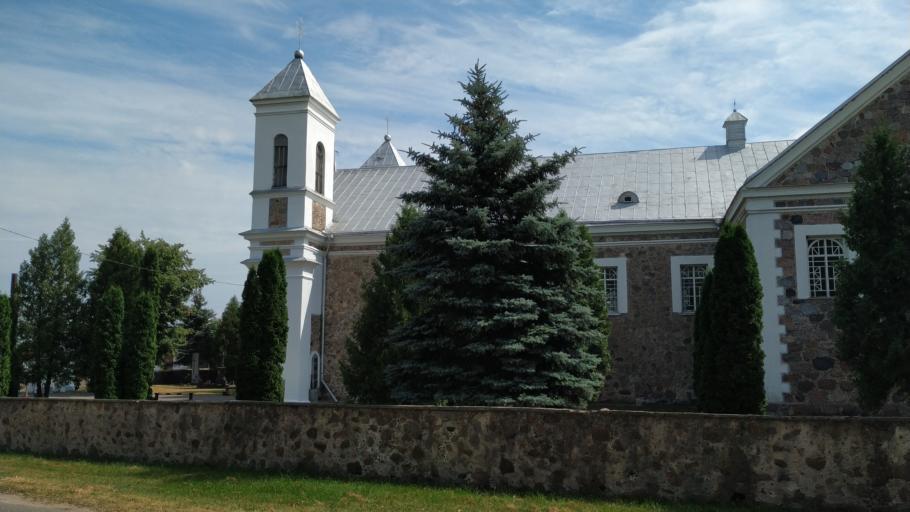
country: LT
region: Vilnius County
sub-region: Trakai
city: Rudiskes
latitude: 54.3580
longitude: 24.8399
